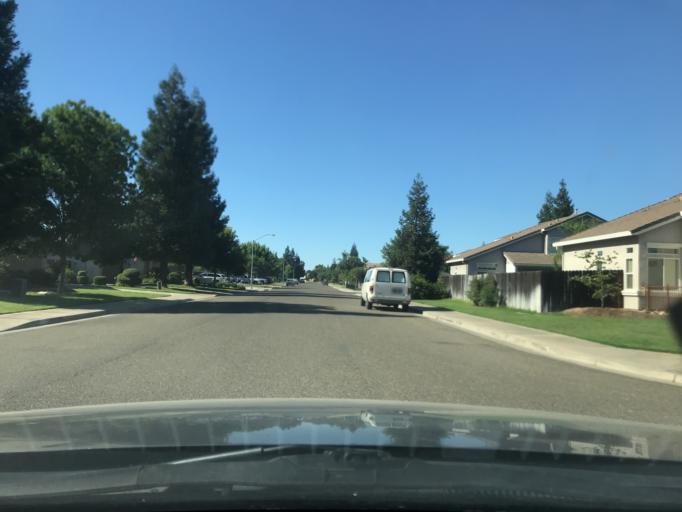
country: US
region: California
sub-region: Merced County
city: Atwater
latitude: 37.3445
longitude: -120.5788
